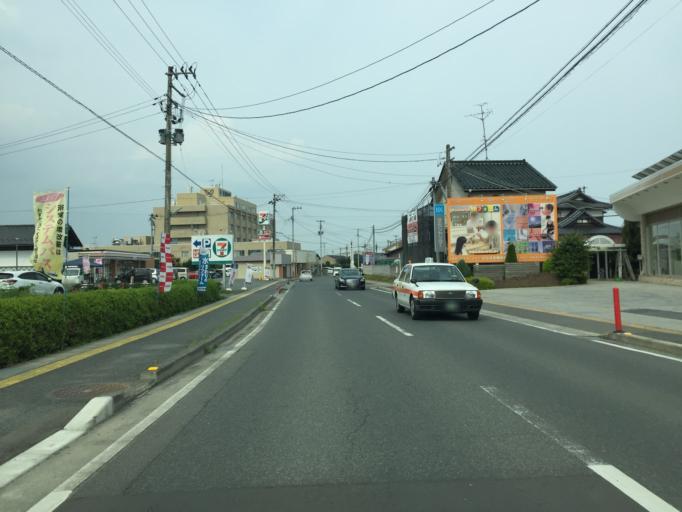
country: JP
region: Fukushima
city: Namie
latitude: 37.6370
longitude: 140.9496
